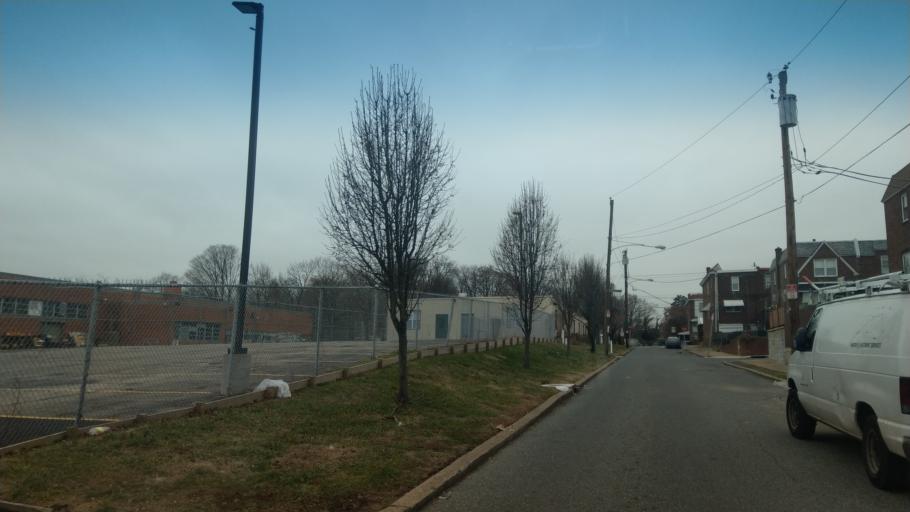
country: US
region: Pennsylvania
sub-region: Montgomery County
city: Rockledge
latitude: 40.0170
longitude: -75.1097
